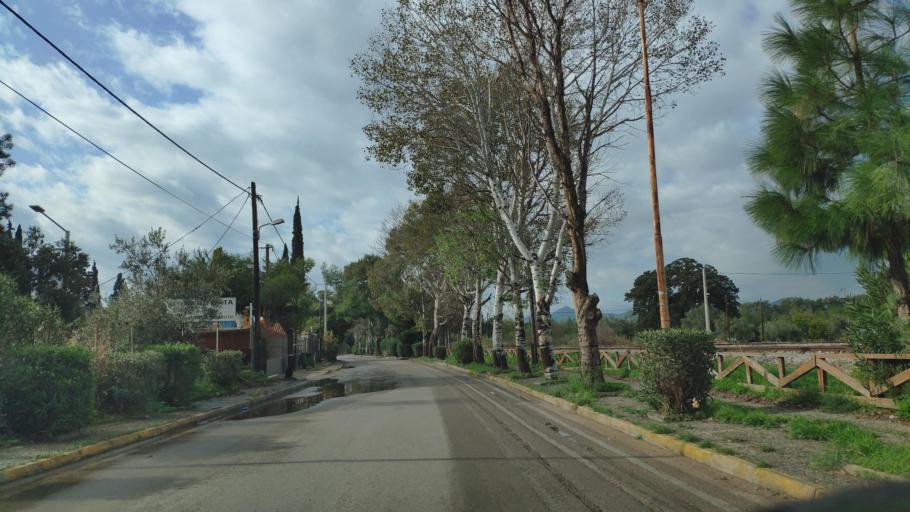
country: GR
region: Attica
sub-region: Nomarchia Dytikis Attikis
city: Elefsina
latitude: 38.0483
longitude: 23.5533
